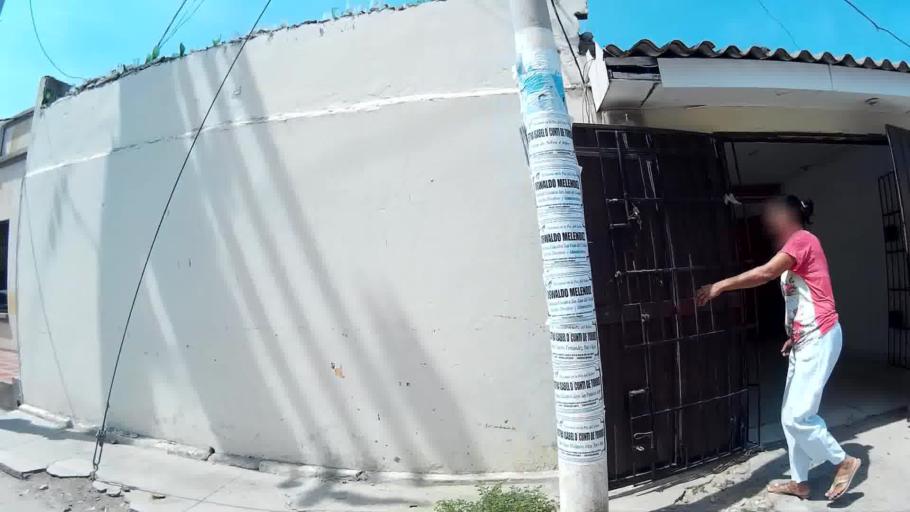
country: CO
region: Magdalena
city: Cienaga
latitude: 11.0107
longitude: -74.2490
